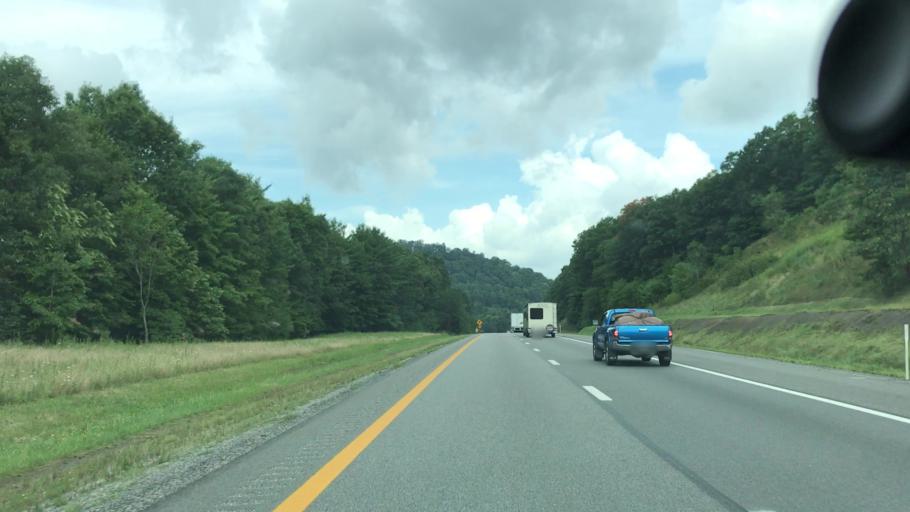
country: US
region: West Virginia
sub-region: Raleigh County
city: Beaver
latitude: 37.7055
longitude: -81.1456
